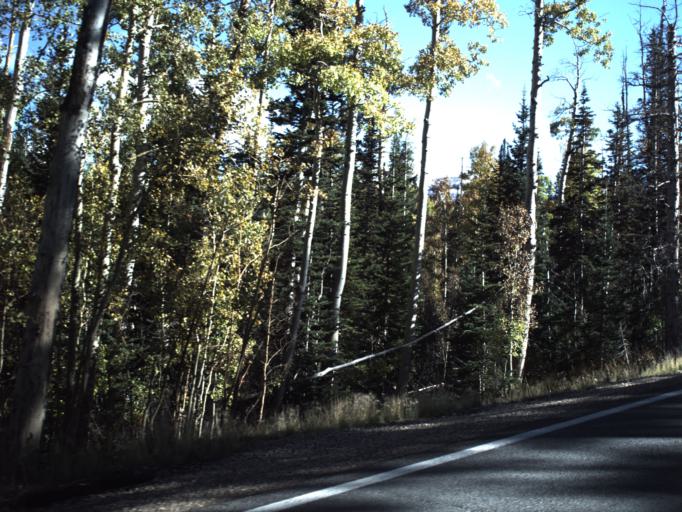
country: US
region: Utah
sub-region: Iron County
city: Parowan
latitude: 37.7082
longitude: -112.8507
